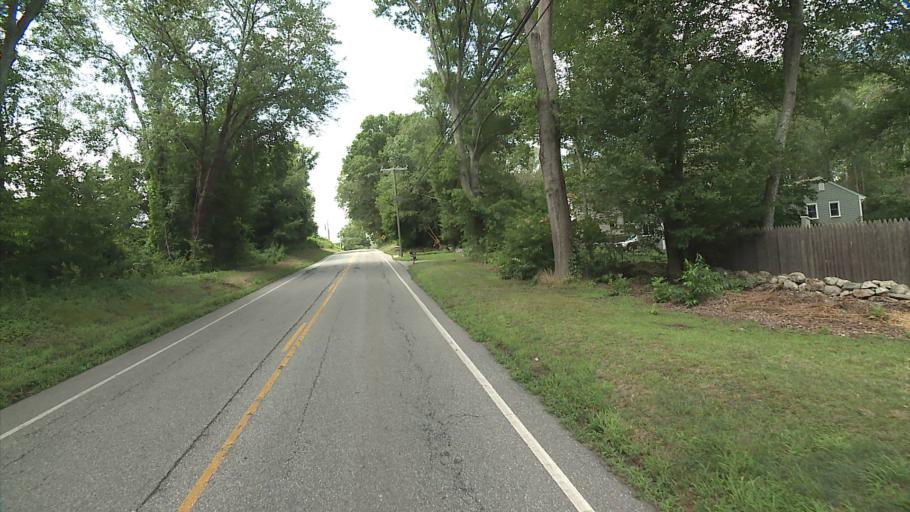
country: US
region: Connecticut
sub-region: New London County
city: Niantic
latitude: 41.3795
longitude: -72.2158
